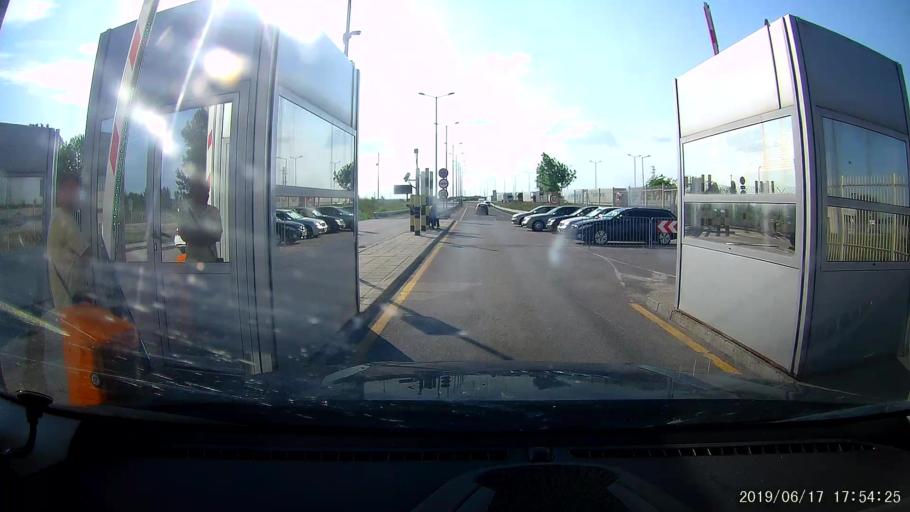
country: GR
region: East Macedonia and Thrace
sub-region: Nomos Evrou
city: Rizia
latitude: 41.7189
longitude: 26.3454
